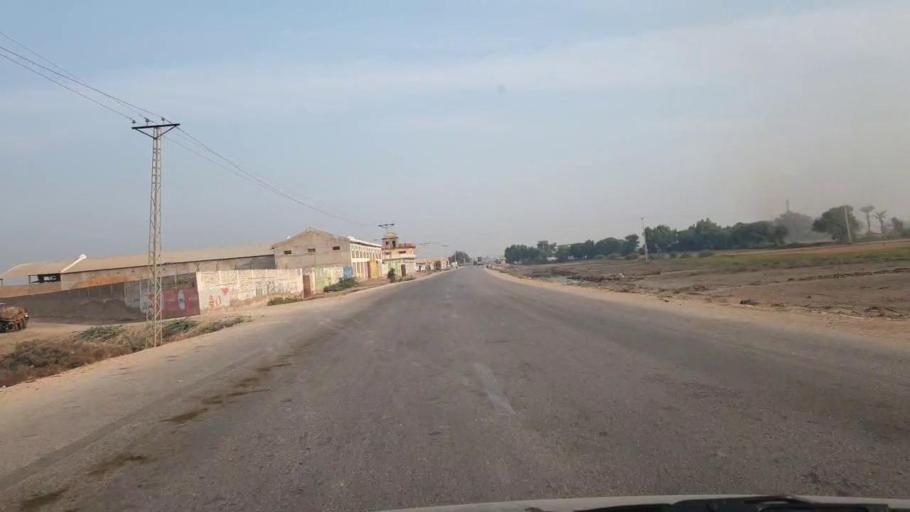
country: PK
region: Sindh
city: Badin
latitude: 24.6854
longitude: 68.8241
